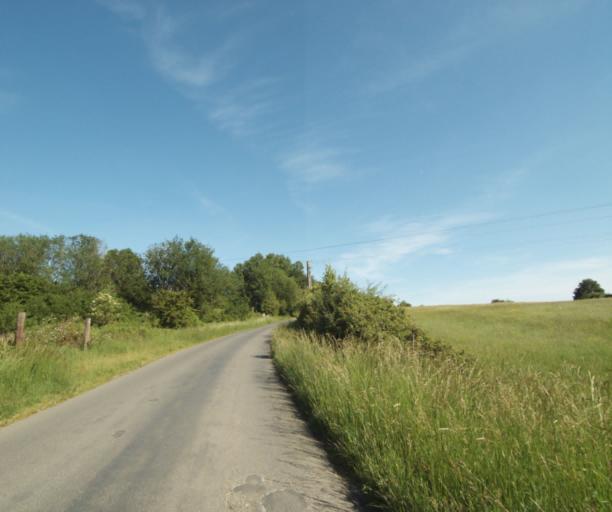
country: FR
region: Champagne-Ardenne
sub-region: Departement des Ardennes
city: Warcq
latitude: 49.7918
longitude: 4.6876
